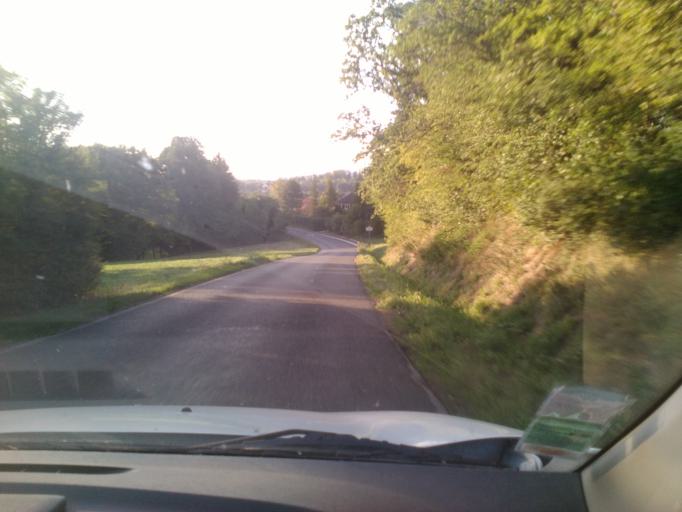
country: FR
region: Lorraine
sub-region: Departement des Vosges
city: Saint-Michel-sur-Meurthe
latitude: 48.3136
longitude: 6.8924
